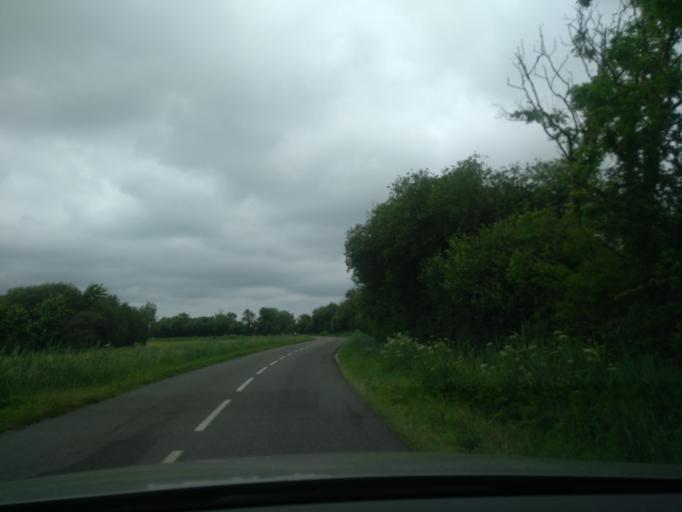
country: FR
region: Lower Normandy
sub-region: Departement de la Manche
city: Sainte-Mere-Eglise
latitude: 49.4644
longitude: -1.2585
